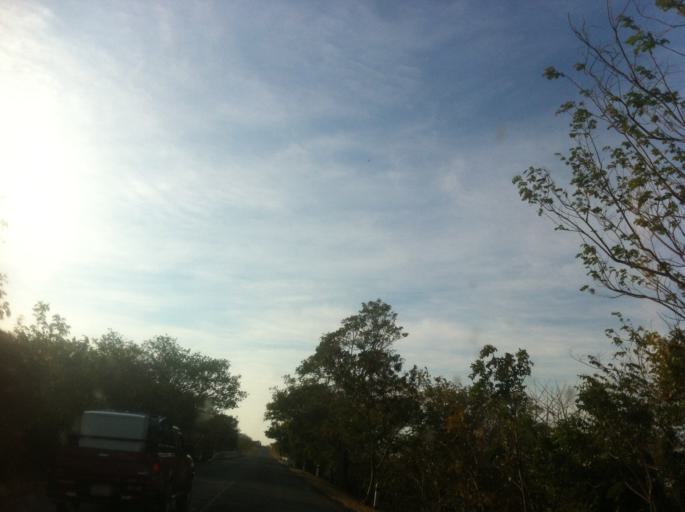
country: NI
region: Rivas
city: Rivas
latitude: 11.3393
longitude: -85.7307
